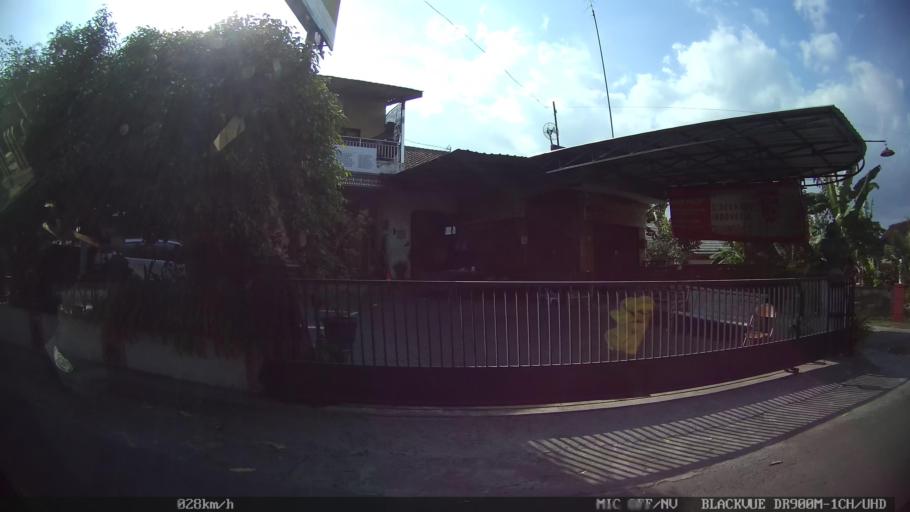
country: ID
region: Daerah Istimewa Yogyakarta
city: Kasihan
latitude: -7.8335
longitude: 110.3378
